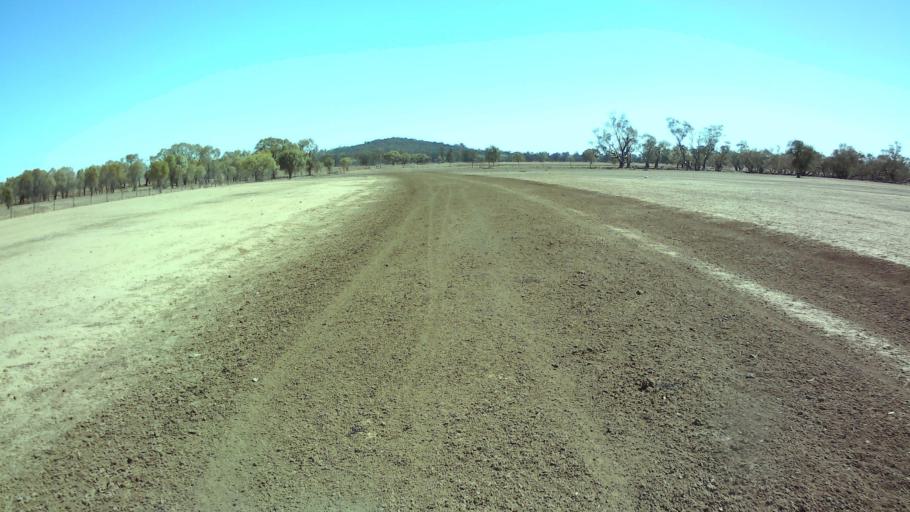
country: AU
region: New South Wales
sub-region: Bland
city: West Wyalong
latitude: -33.7524
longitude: 147.6597
